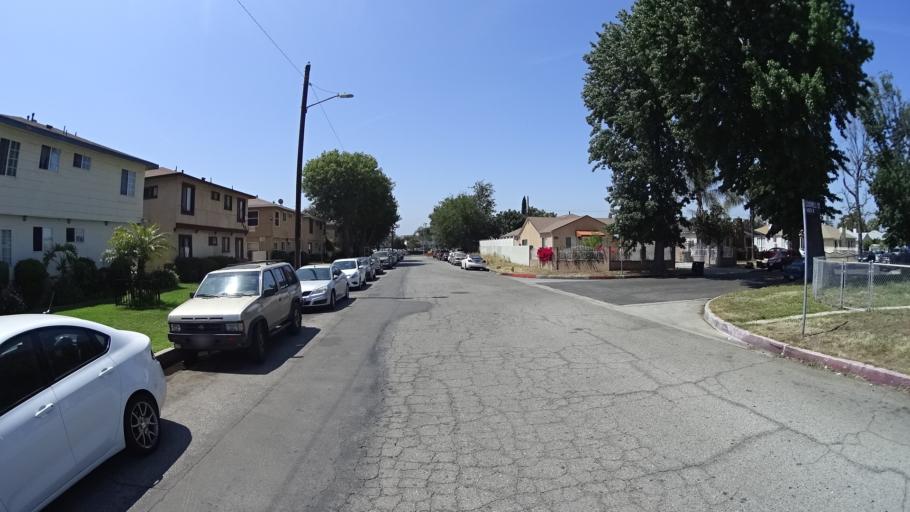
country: US
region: California
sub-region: Los Angeles County
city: Van Nuys
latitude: 34.2041
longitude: -118.4500
